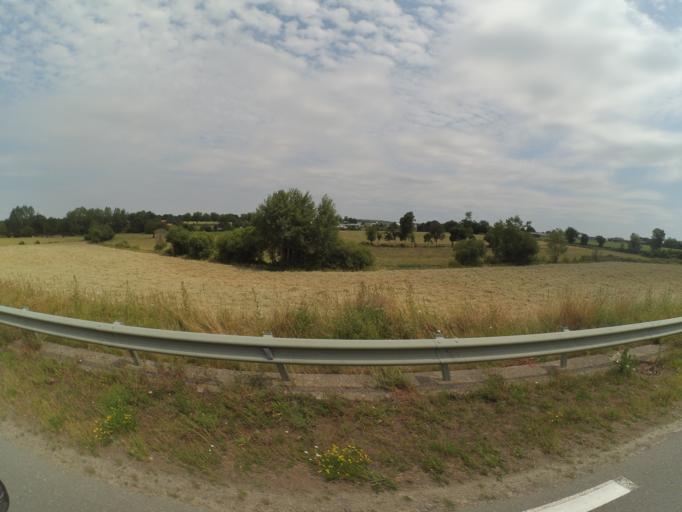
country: FR
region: Pays de la Loire
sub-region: Departement de la Vendee
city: Les Herbiers
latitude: 46.8491
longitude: -1.0541
